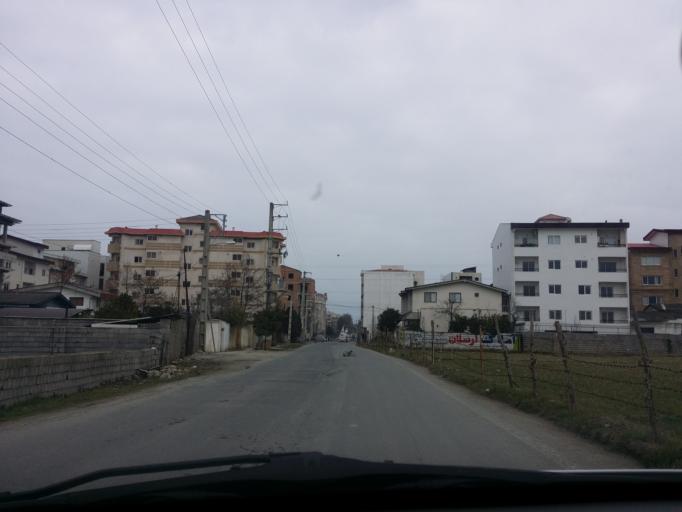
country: IR
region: Mazandaran
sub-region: Nowshahr
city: Nowshahr
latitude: 36.6480
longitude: 51.4842
